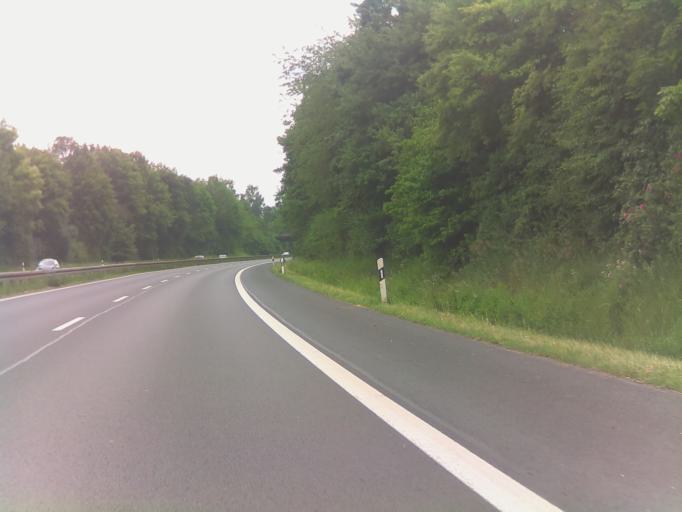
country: DE
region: Hesse
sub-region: Regierungsbezirk Kassel
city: Eichenzell
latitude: 50.5135
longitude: 9.6858
